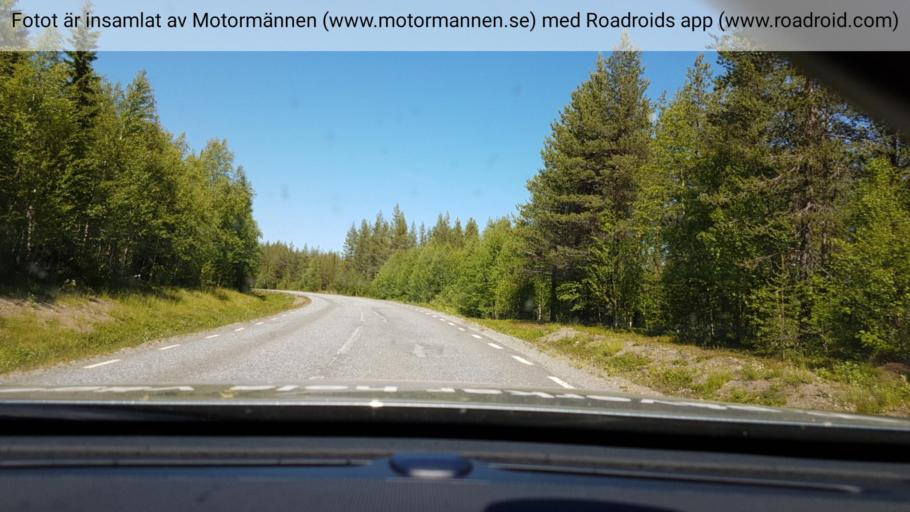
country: SE
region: Vaesterbotten
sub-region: Vilhelmina Kommun
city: Sjoberg
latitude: 64.8649
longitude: 15.8964
